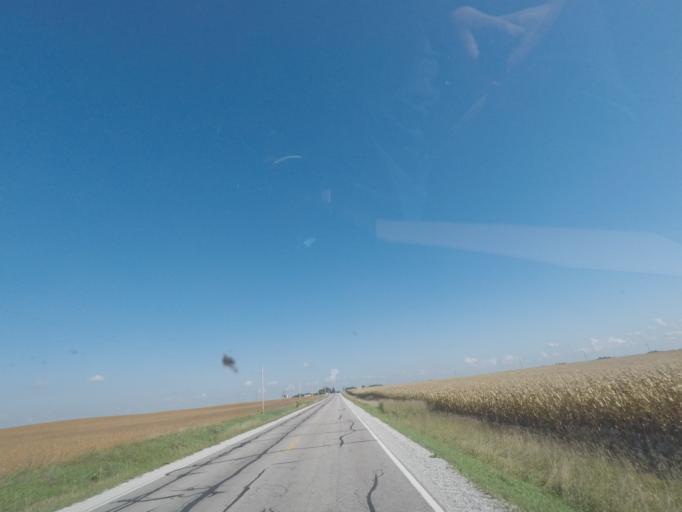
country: US
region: Iowa
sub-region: Story County
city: Nevada
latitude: 42.0304
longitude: -93.4057
